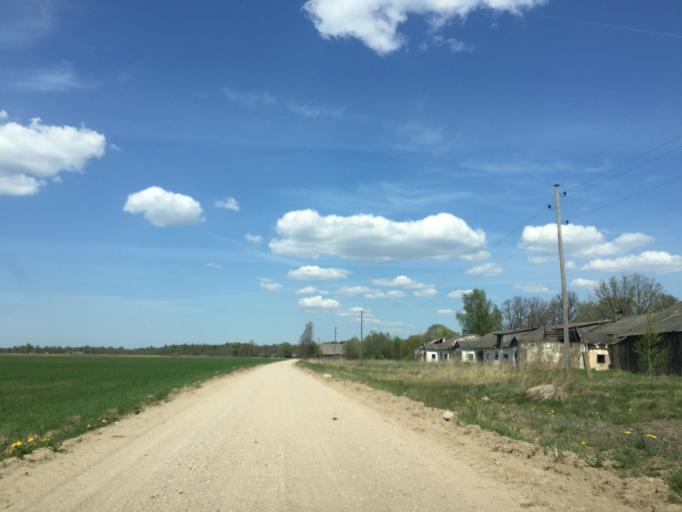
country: LV
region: Limbazu Rajons
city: Limbazi
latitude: 57.3709
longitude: 24.6336
